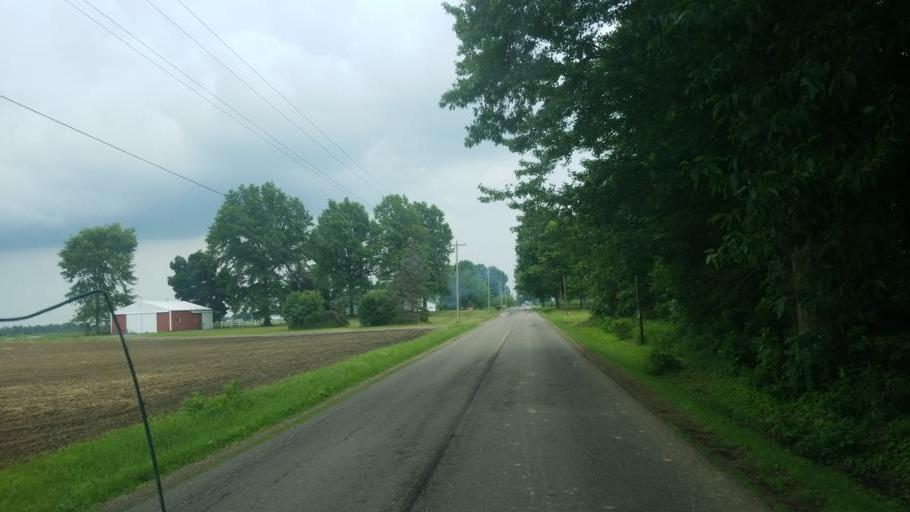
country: US
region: Ohio
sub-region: Wayne County
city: Smithville
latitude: 40.9014
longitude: -81.8889
